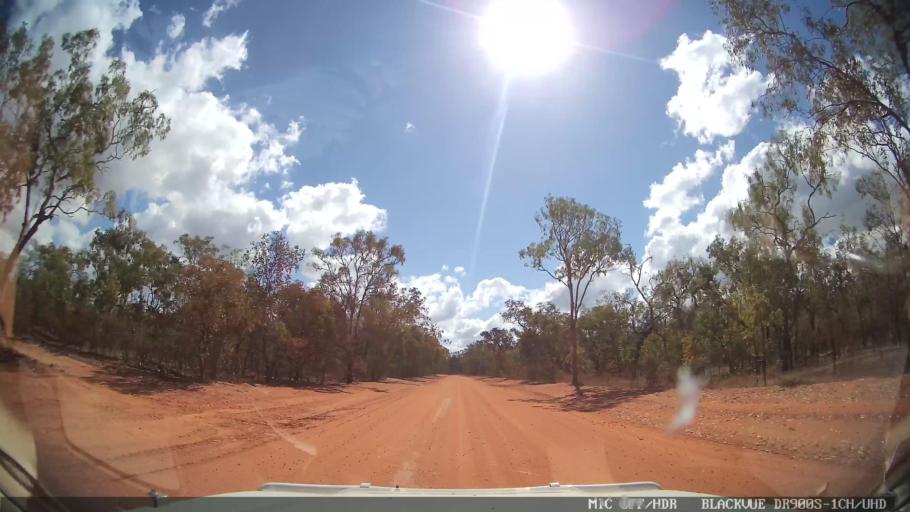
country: AU
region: Queensland
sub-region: Cook
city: Cooktown
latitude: -15.1928
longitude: 144.3752
